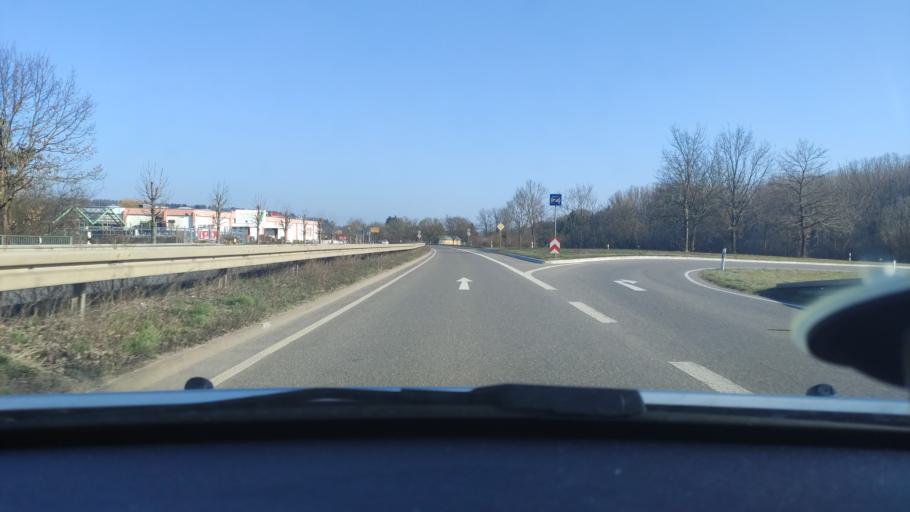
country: DE
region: Baden-Wuerttemberg
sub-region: Tuebingen Region
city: Balingen
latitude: 48.2564
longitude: 8.8557
